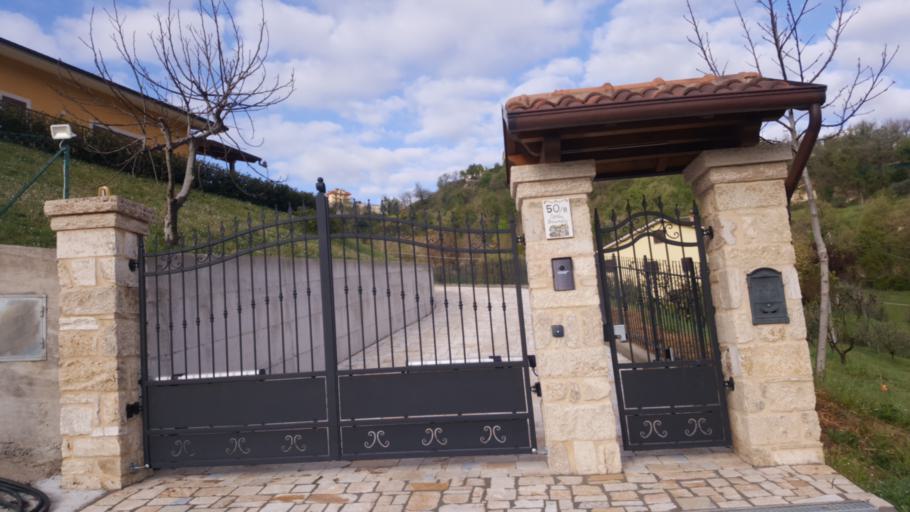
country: IT
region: The Marches
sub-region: Provincia di Ascoli Piceno
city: Venarotta
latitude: 42.8677
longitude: 13.5336
